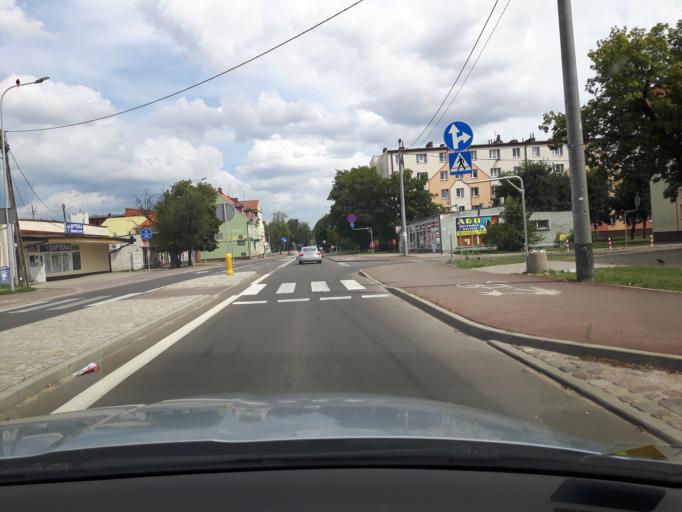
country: PL
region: Warmian-Masurian Voivodeship
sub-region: Powiat nidzicki
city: Nidzica
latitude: 53.3615
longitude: 20.4218
